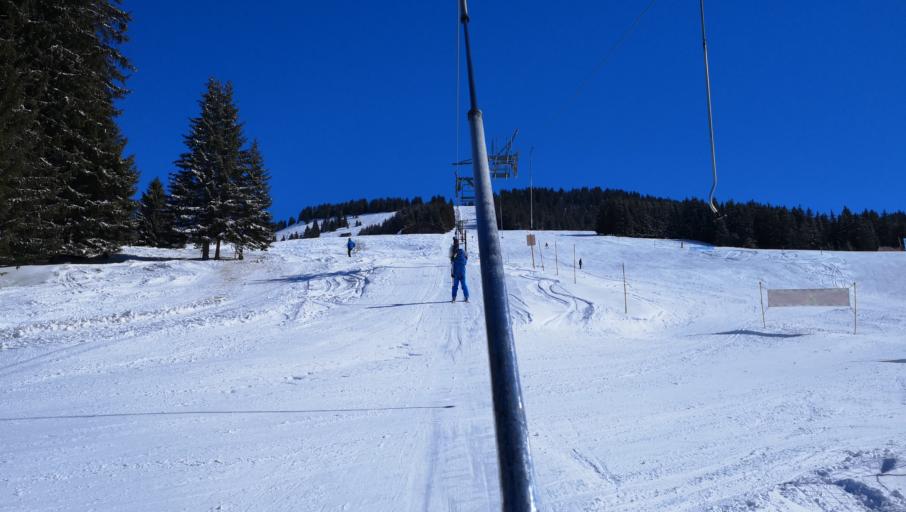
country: FR
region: Rhone-Alpes
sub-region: Departement de la Haute-Savoie
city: Megeve
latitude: 45.8456
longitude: 6.6544
